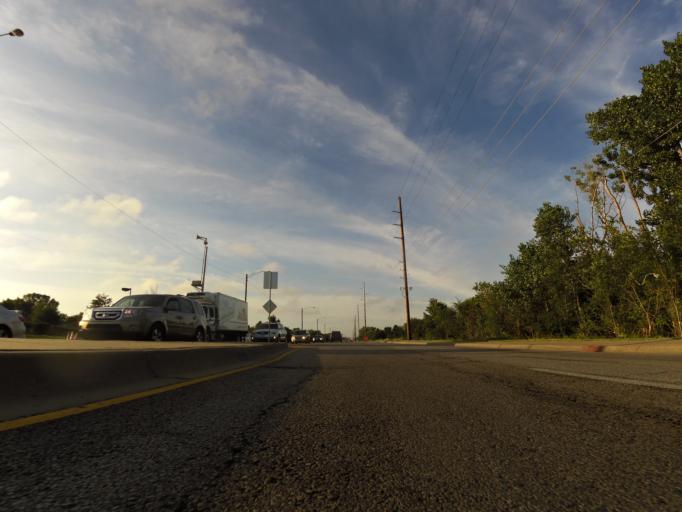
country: US
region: Kansas
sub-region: Sedgwick County
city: Bellaire
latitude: 37.7431
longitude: -97.2624
